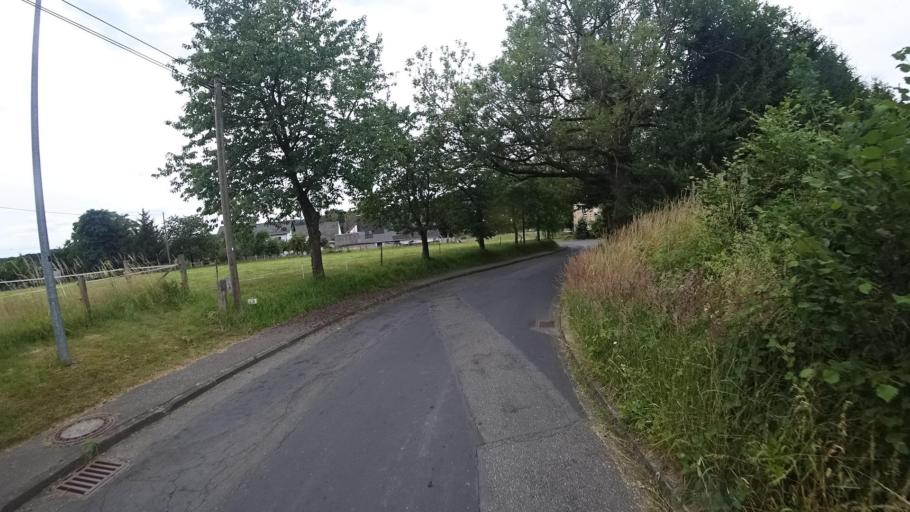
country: DE
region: Rheinland-Pfalz
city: Giershausen
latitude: 50.6806
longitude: 7.5484
